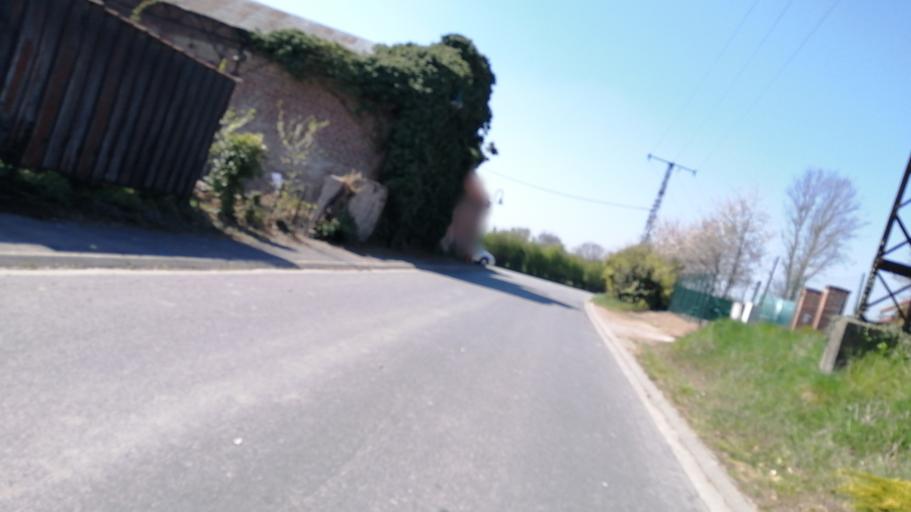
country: FR
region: Nord-Pas-de-Calais
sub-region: Departement du Pas-de-Calais
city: Mont-Saint-Eloi
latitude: 50.3451
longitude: 2.6708
